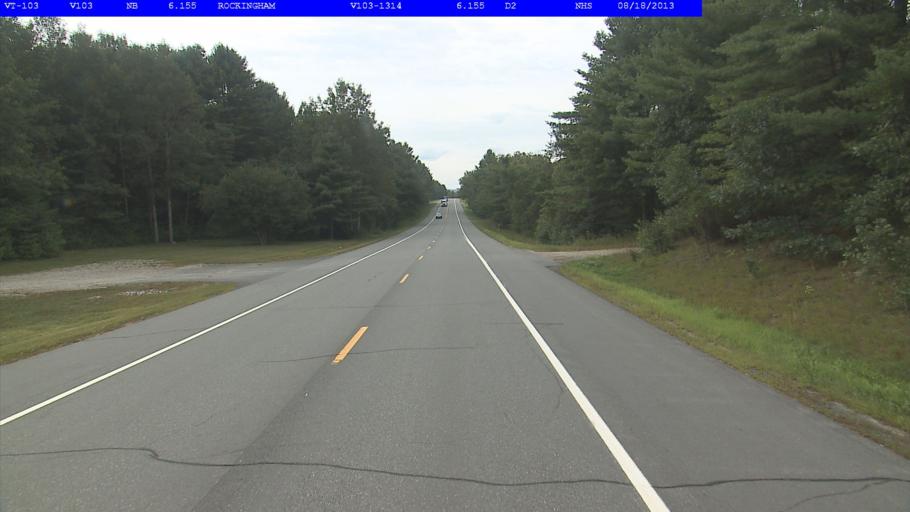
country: US
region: Vermont
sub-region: Windsor County
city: Chester
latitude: 43.2289
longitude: -72.5450
